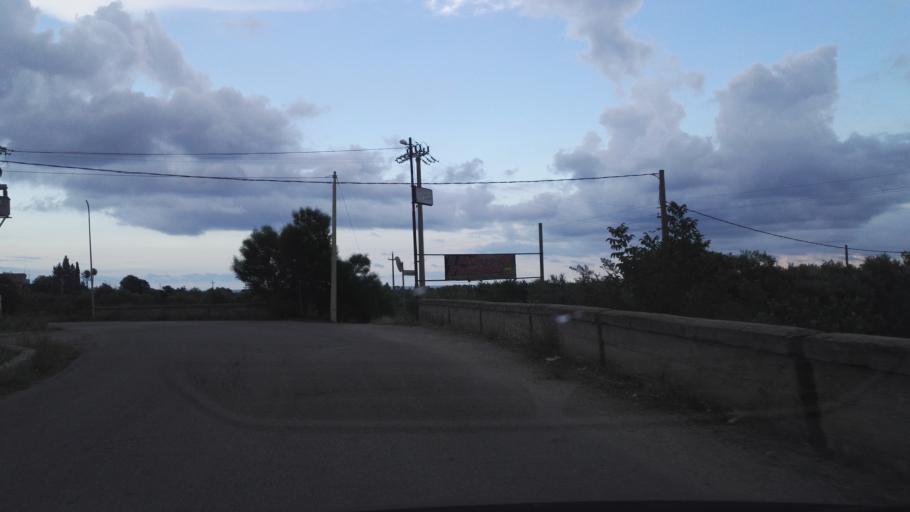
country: IT
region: Calabria
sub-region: Provincia di Reggio Calabria
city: Caulonia Marina
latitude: 38.3622
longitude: 16.4608
